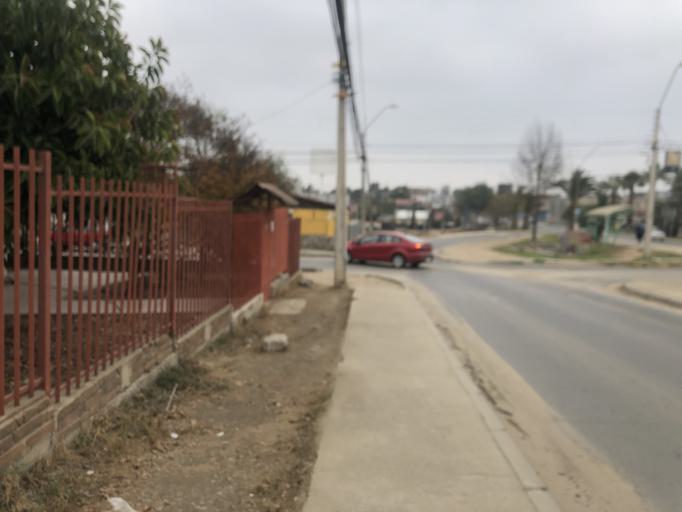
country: CL
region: Valparaiso
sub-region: Provincia de Marga Marga
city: Quilpue
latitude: -33.0488
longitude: -71.4277
